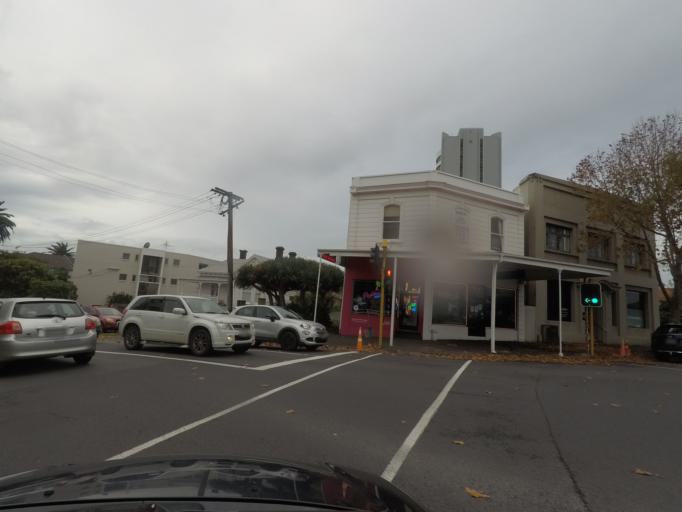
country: NZ
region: Auckland
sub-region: Auckland
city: Auckland
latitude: -36.8450
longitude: 174.7402
